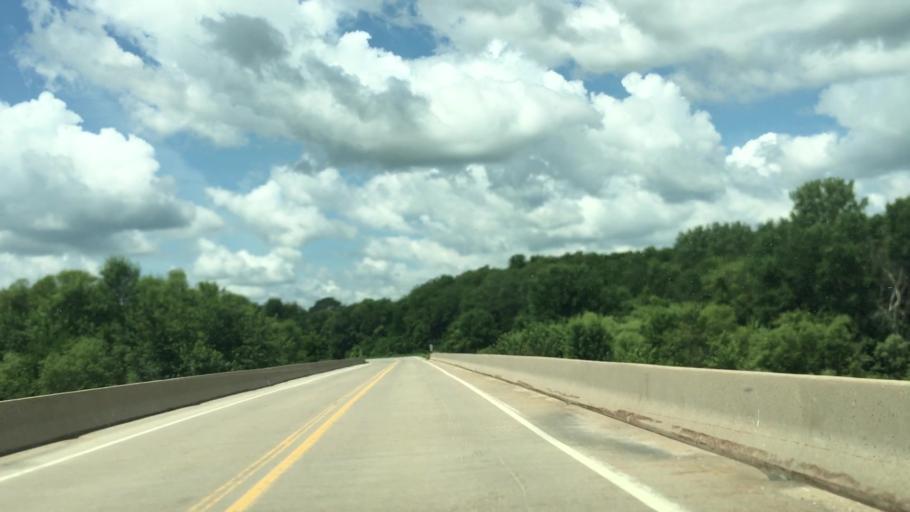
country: US
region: Iowa
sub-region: Linn County
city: Lisbon
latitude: 41.8451
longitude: -91.3910
